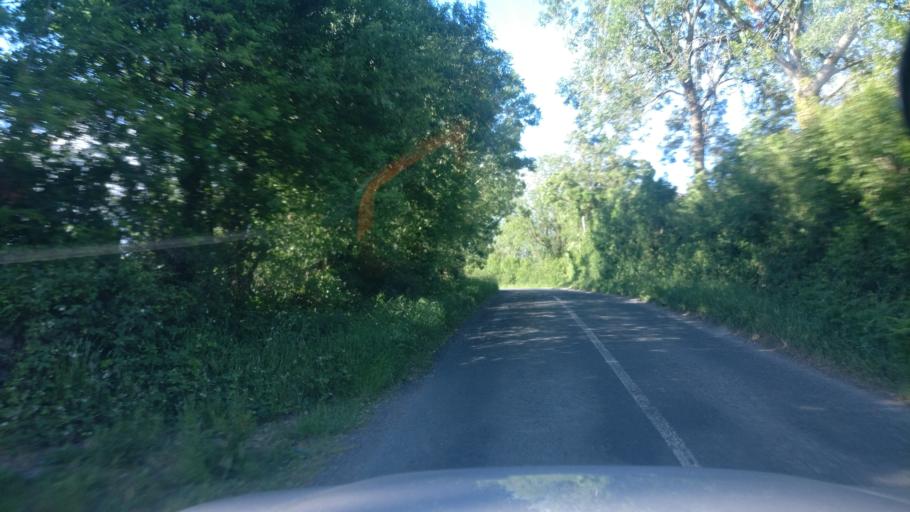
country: IE
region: Connaught
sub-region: County Galway
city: Ballinasloe
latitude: 53.2221
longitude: -8.2917
